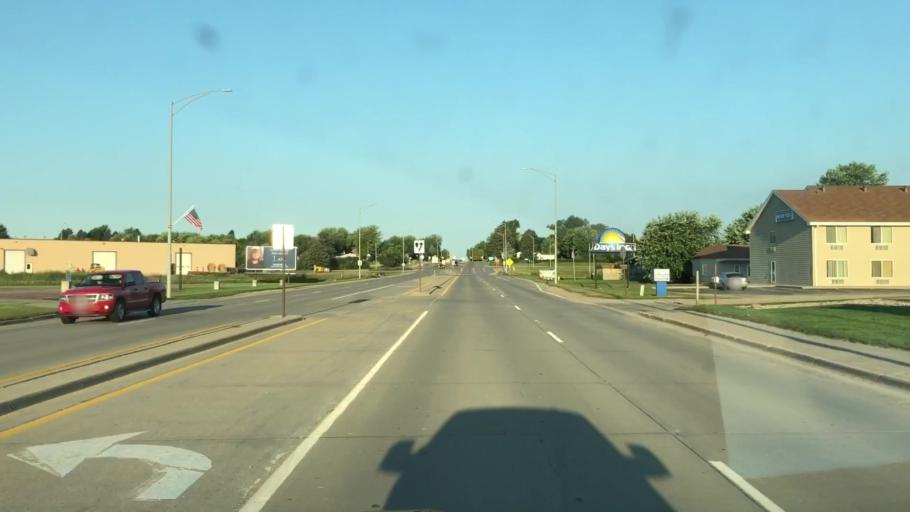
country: US
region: Minnesota
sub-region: Nobles County
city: Worthington
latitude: 43.6312
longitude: -95.6098
